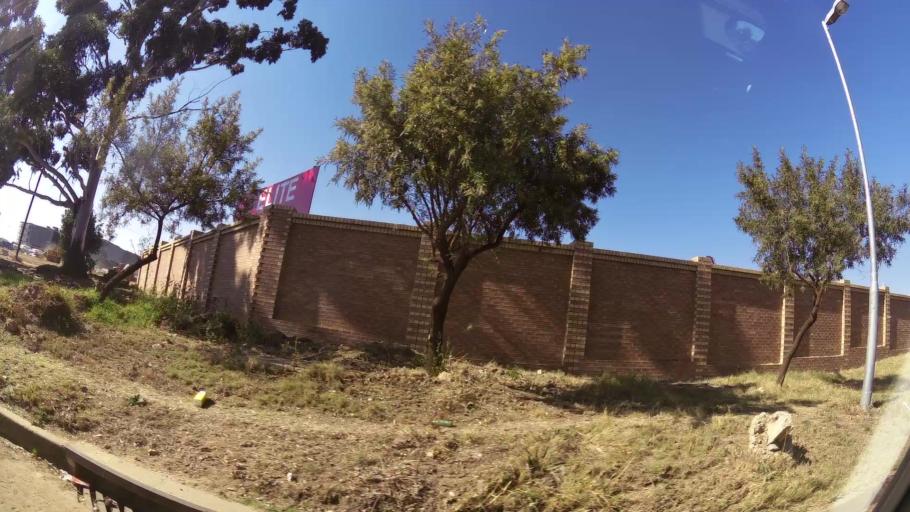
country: ZA
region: Gauteng
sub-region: City of Johannesburg Metropolitan Municipality
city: Midrand
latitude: -25.9631
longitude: 28.1283
